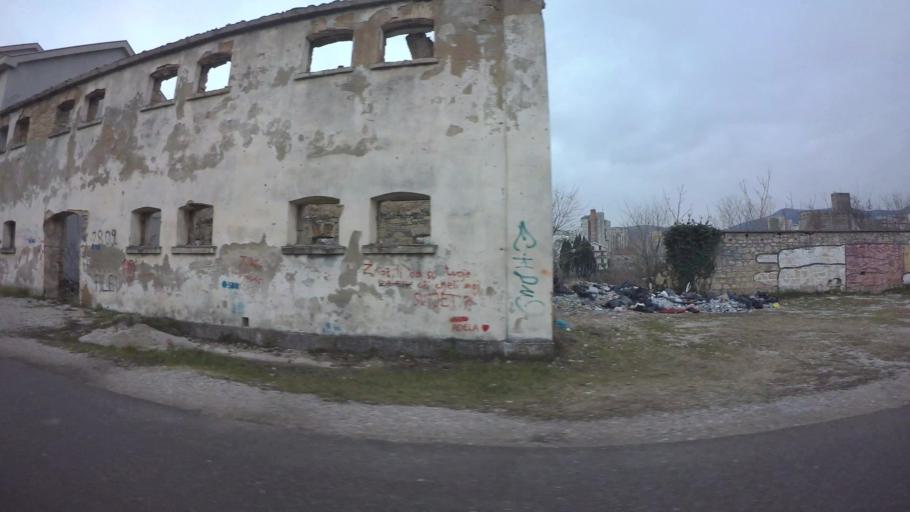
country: BA
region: Federation of Bosnia and Herzegovina
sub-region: Hercegovacko-Bosanski Kanton
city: Mostar
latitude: 43.3539
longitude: 17.8085
